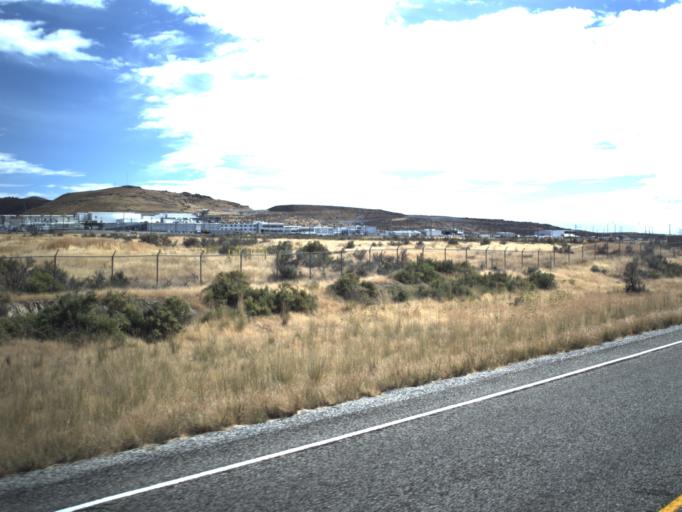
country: US
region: Utah
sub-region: Box Elder County
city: Tremonton
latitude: 41.6662
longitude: -112.4451
